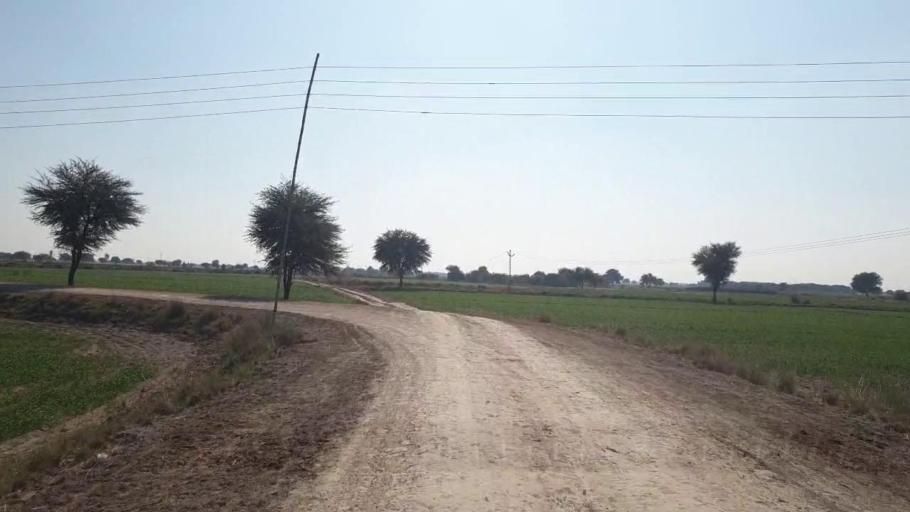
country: PK
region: Sindh
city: Shahdadpur
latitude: 25.9516
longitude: 68.6557
